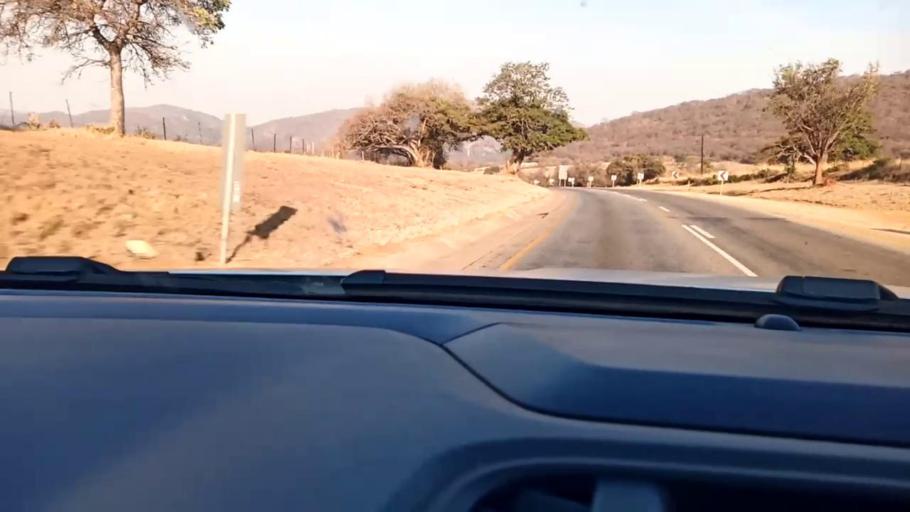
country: ZA
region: Limpopo
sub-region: Mopani District Municipality
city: Duiwelskloof
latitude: -23.6430
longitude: 30.1609
